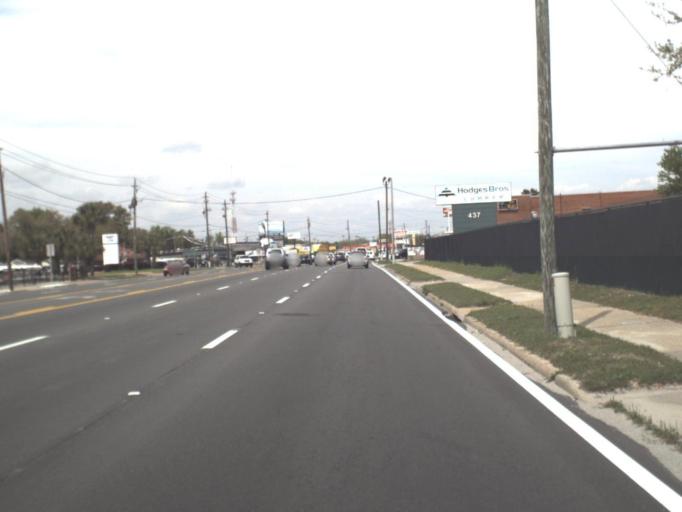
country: US
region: Florida
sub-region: Okaloosa County
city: Ocean City
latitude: 30.4372
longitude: -86.6015
